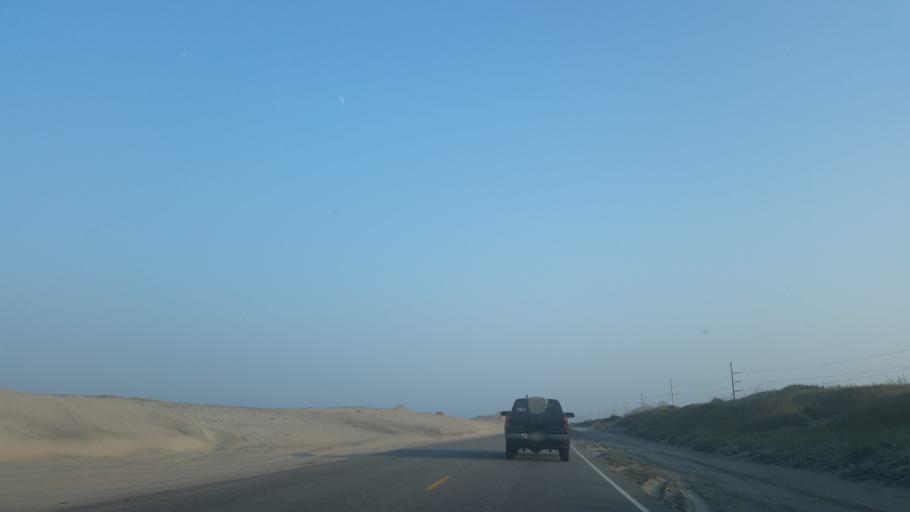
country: US
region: North Carolina
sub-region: Dare County
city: Wanchese
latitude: 35.7543
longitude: -75.5108
